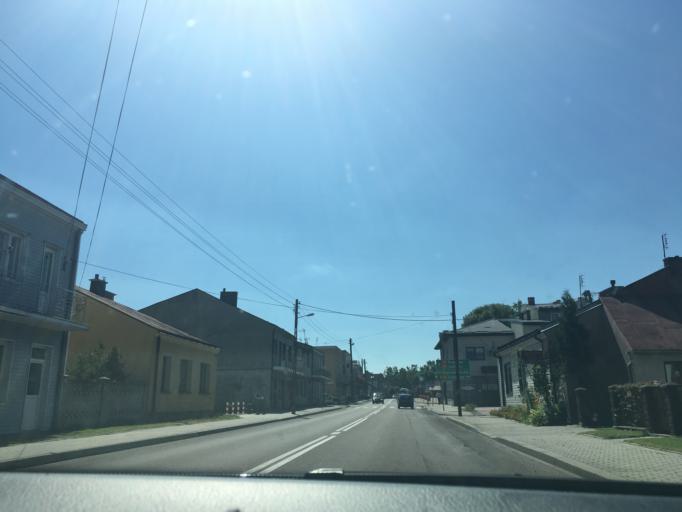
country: PL
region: Lublin Voivodeship
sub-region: Powiat janowski
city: Modliborzyce
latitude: 50.7548
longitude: 22.3290
